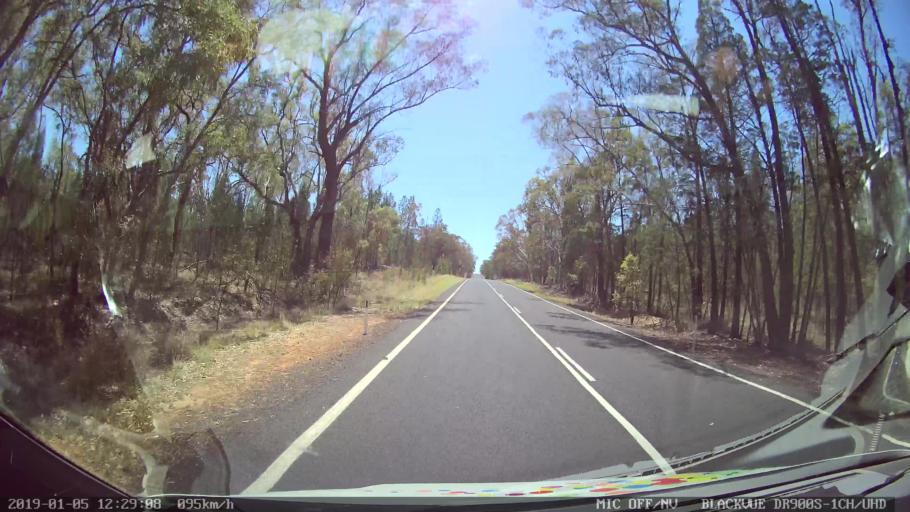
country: AU
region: New South Wales
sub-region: Warrumbungle Shire
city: Coonabarabran
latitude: -31.2353
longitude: 149.3330
